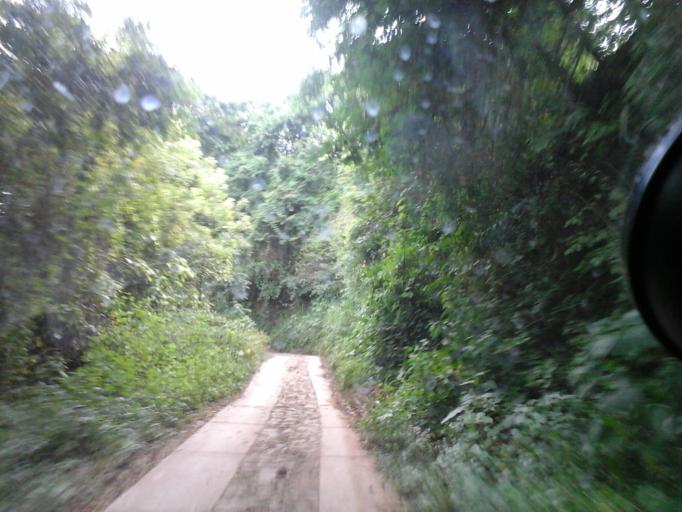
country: CO
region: Cesar
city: San Diego
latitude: 10.2646
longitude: -73.1040
